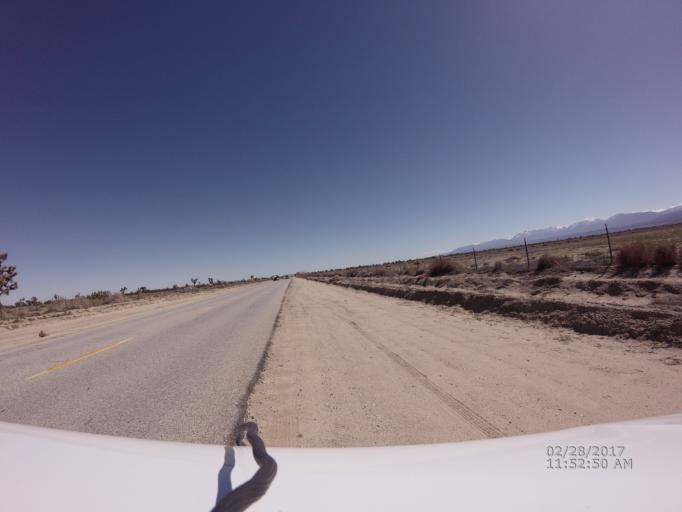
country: US
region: California
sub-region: Los Angeles County
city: Palmdale
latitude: 34.6020
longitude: -118.0503
